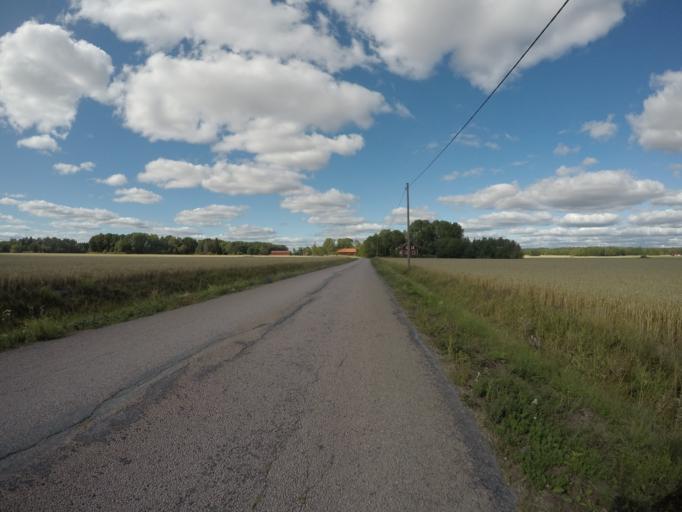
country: SE
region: Vaestmanland
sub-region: Hallstahammars Kommun
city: Kolback
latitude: 59.5095
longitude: 16.1899
